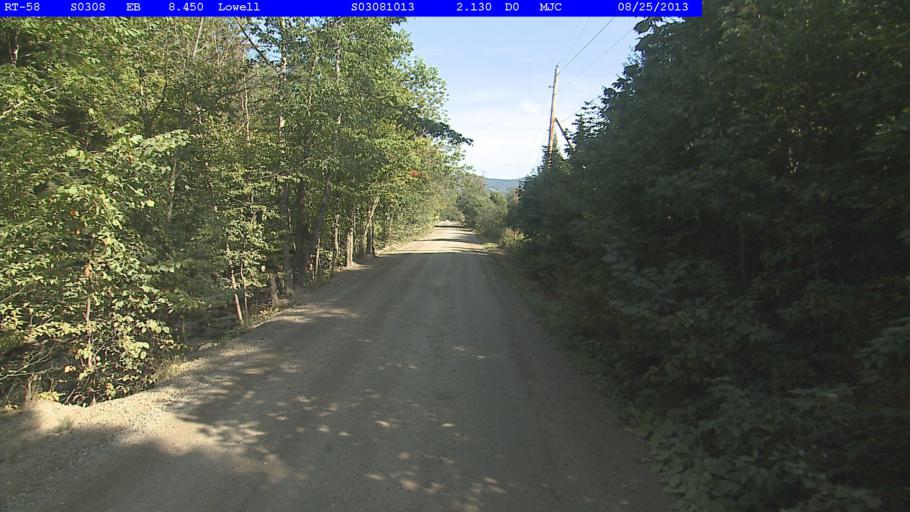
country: US
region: Vermont
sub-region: Lamoille County
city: Hyde Park
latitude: 44.8178
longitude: -72.4743
